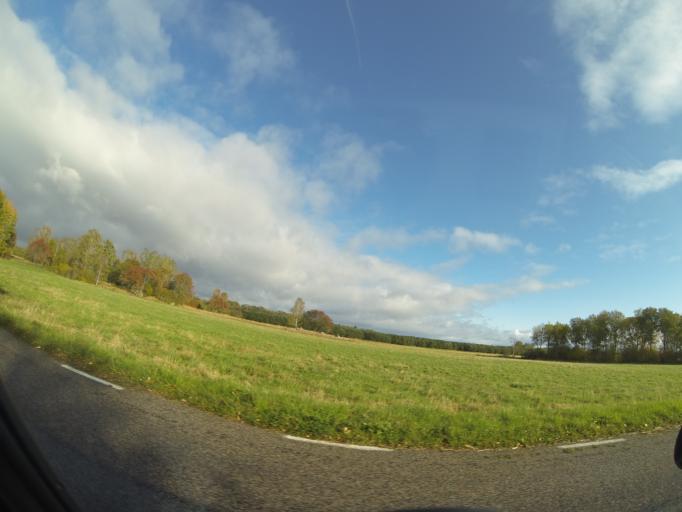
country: SE
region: Soedermanland
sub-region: Eskilstuna Kommun
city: Kvicksund
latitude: 59.3444
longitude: 16.2545
